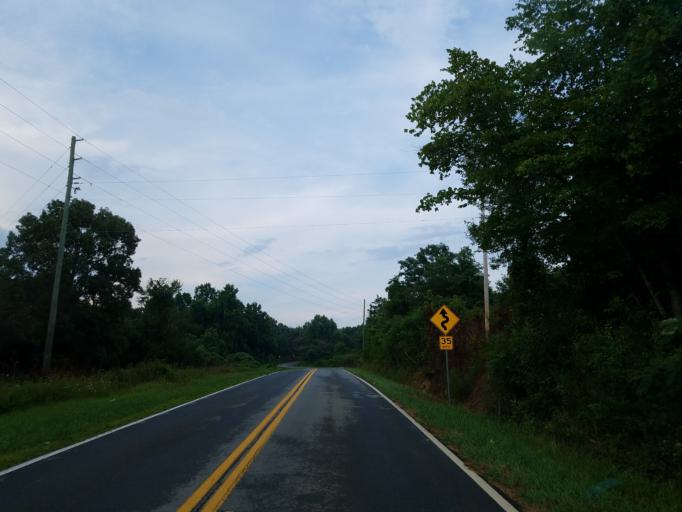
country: US
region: Georgia
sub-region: Pickens County
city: Jasper
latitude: 34.4554
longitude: -84.5448
